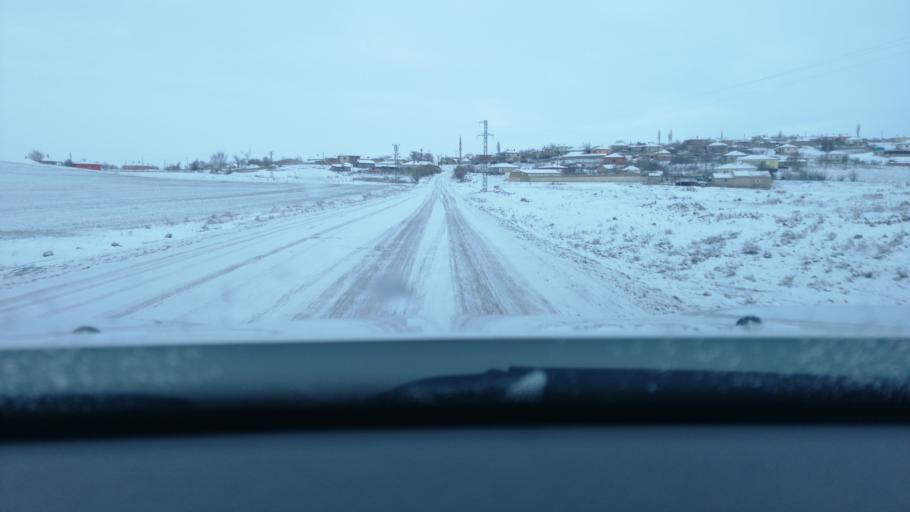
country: TR
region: Aksaray
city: Agacoren
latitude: 38.9393
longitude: 33.9479
